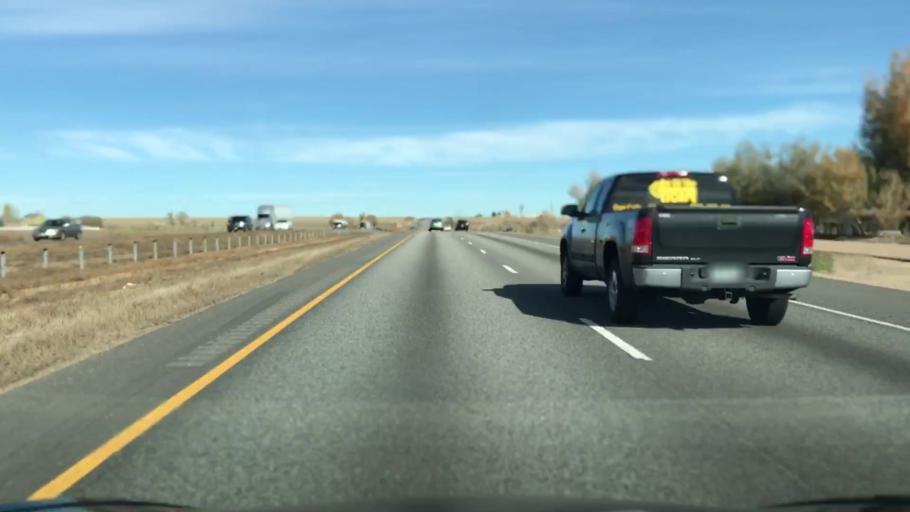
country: US
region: Colorado
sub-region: Weld County
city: Mead
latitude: 40.2526
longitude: -104.9801
